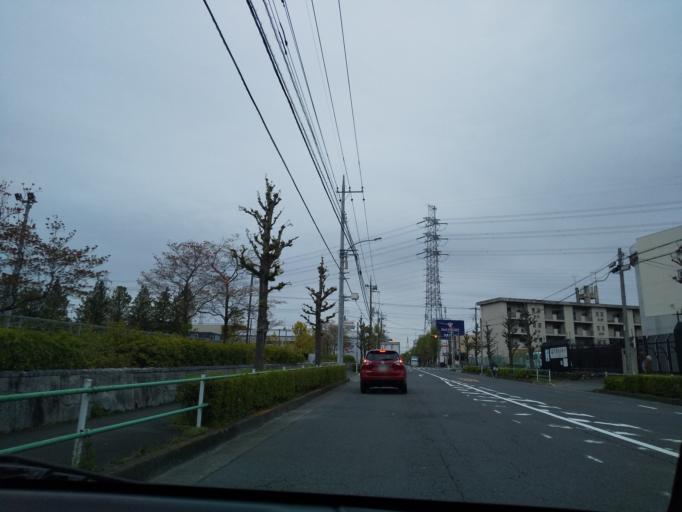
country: JP
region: Tokyo
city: Hino
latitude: 35.6623
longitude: 139.3680
